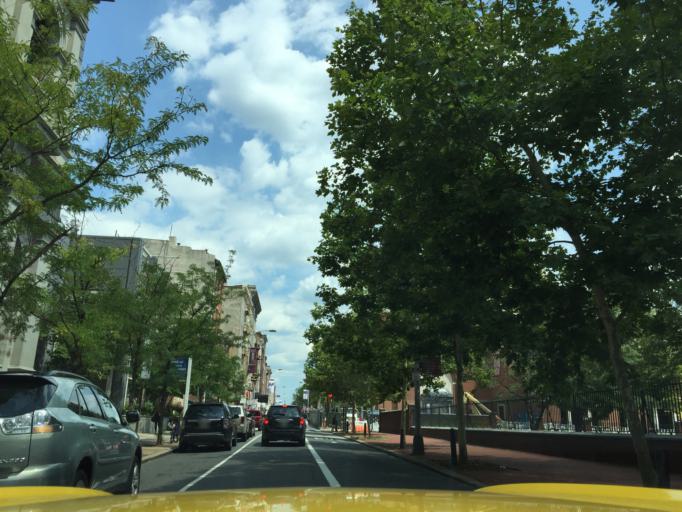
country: US
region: Pennsylvania
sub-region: Philadelphia County
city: Philadelphia
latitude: 39.9487
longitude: -75.1469
